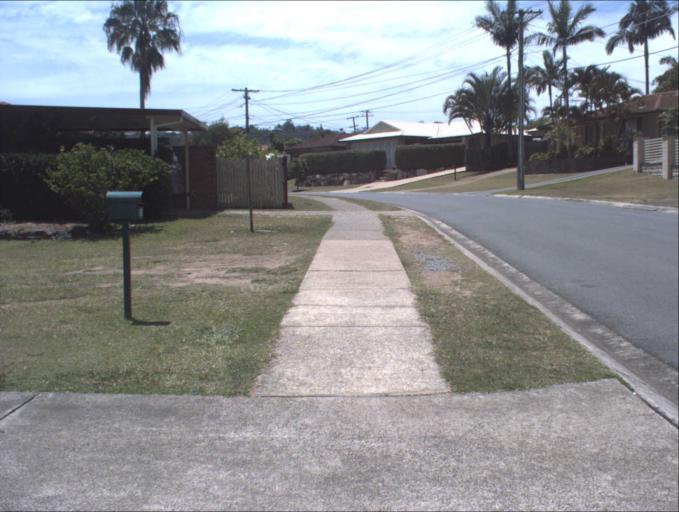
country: AU
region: Queensland
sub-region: Logan
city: Slacks Creek
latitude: -27.6380
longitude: 153.1406
